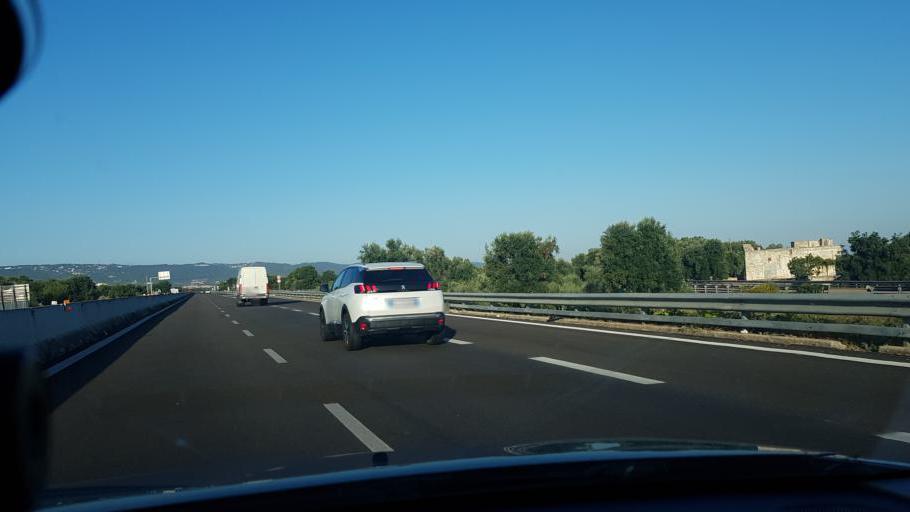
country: IT
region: Apulia
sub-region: Provincia di Brindisi
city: Pezze di Greco
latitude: 40.8338
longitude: 17.4076
